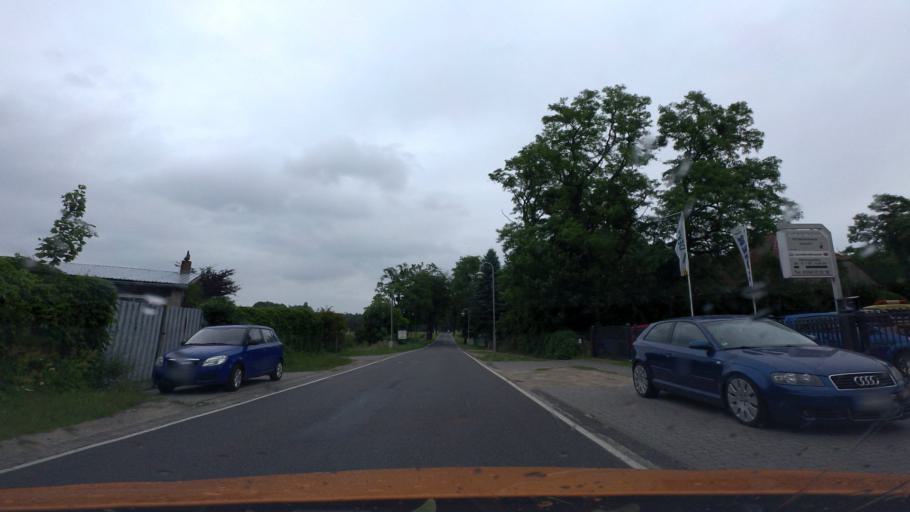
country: DE
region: Brandenburg
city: Strausberg
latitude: 52.6050
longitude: 13.8758
